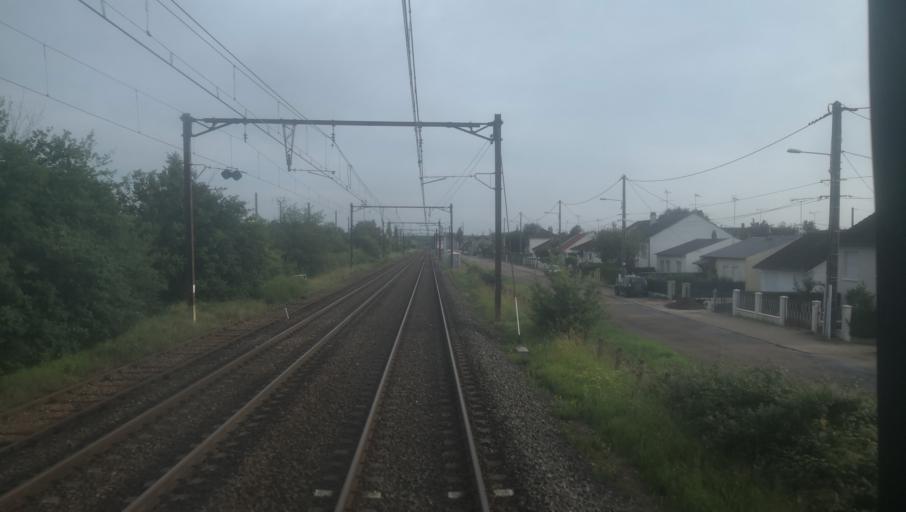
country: FR
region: Centre
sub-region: Departement du Loiret
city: La Ferte-Saint-Aubin
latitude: 47.7154
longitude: 1.9338
